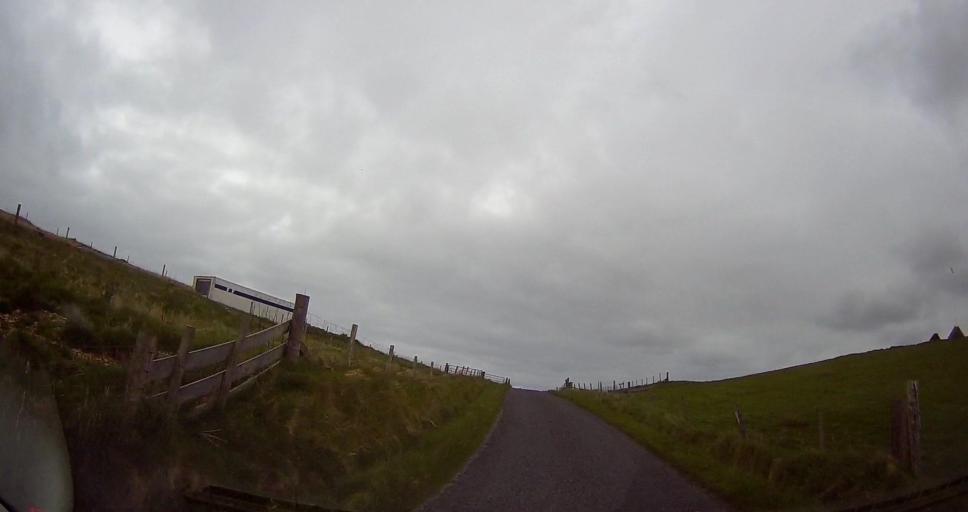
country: GB
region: Scotland
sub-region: Shetland Islands
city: Shetland
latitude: 60.8006
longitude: -0.8750
